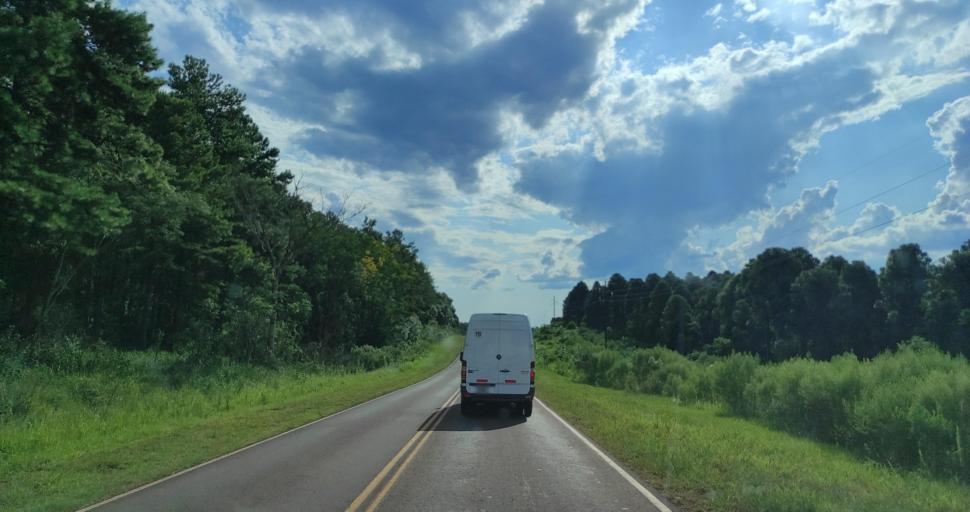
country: AR
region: Misiones
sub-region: Departamento de San Pedro
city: San Pedro
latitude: -26.3481
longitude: -53.9753
